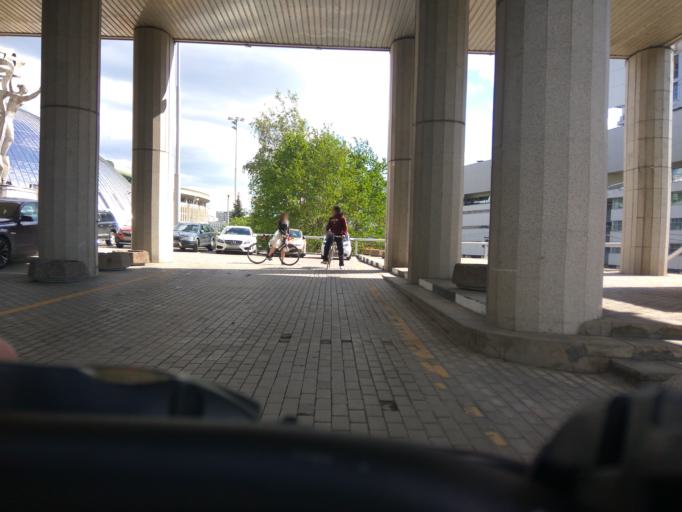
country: RU
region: Moscow
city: Mar'ina Roshcha
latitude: 55.7853
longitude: 37.6230
